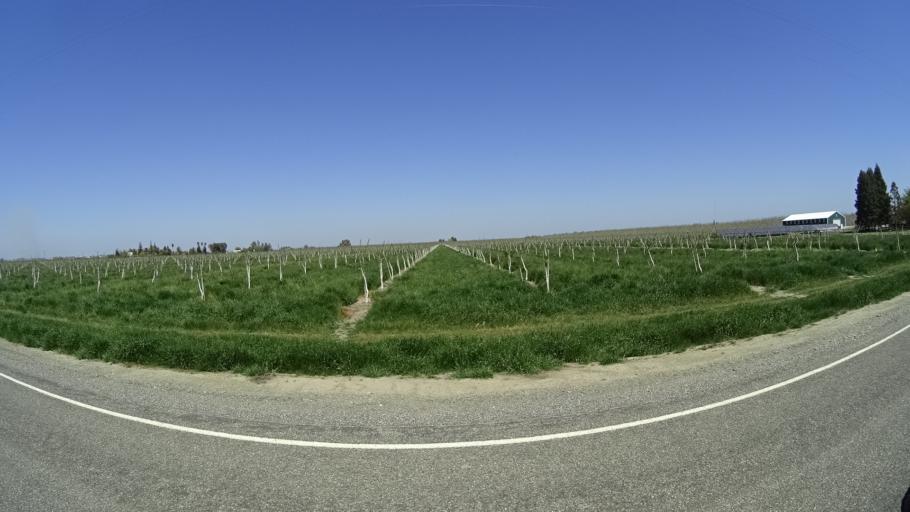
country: US
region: California
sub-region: Glenn County
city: Willows
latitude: 39.5579
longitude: -122.0139
